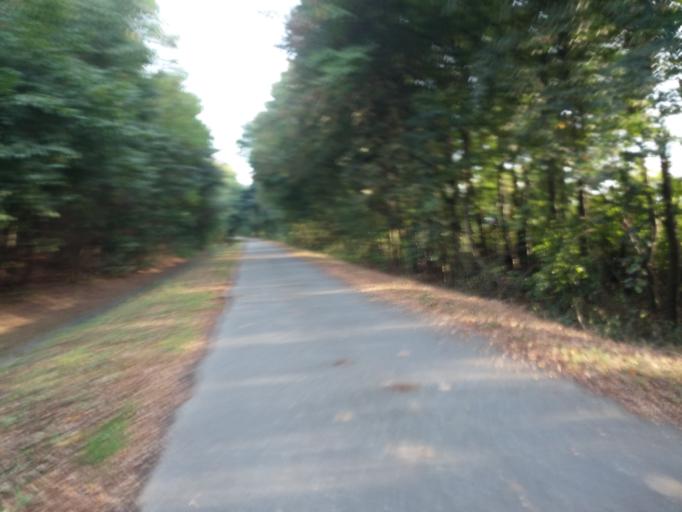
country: DE
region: North Rhine-Westphalia
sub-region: Regierungsbezirk Munster
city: Gladbeck
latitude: 51.6153
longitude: 7.0207
